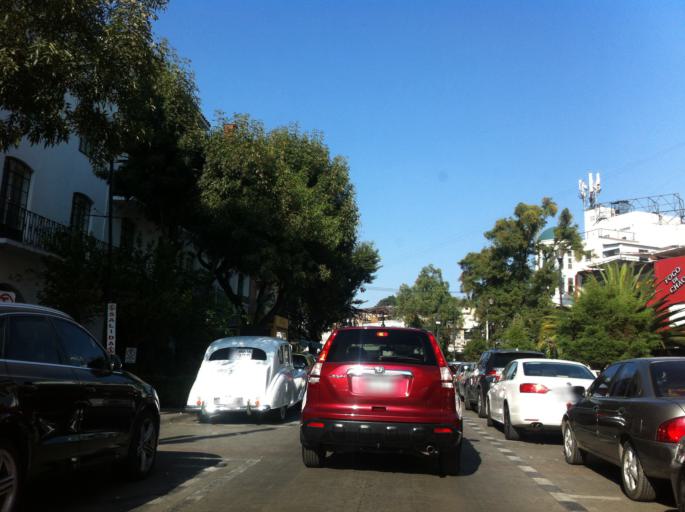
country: MX
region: Mexico City
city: Miguel Hidalgo
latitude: 19.4309
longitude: -99.1962
